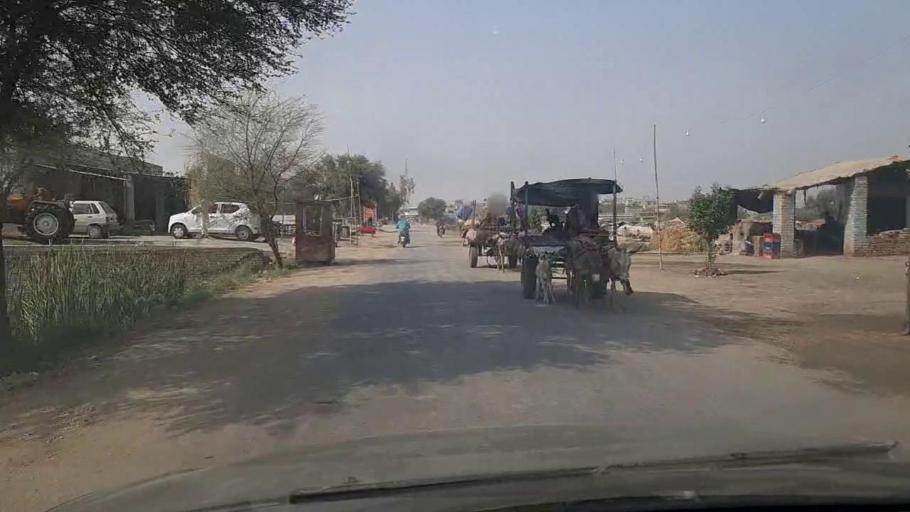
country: PK
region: Sindh
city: Mirpur Mathelo
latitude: 27.9196
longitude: 69.5243
